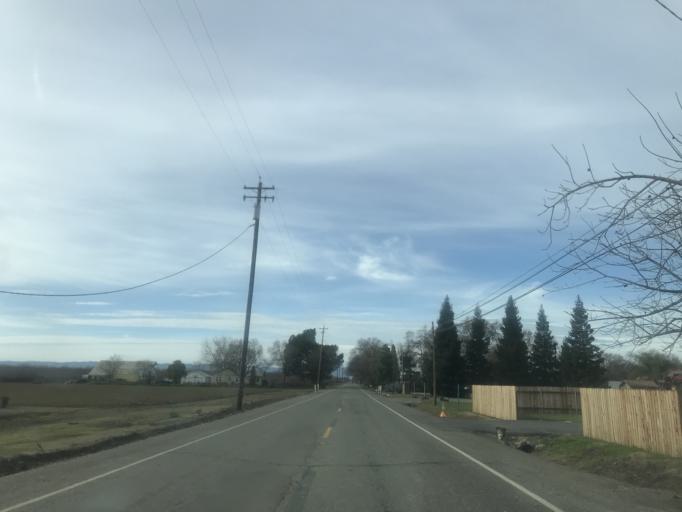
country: US
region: California
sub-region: Yolo County
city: Woodland
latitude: 38.6633
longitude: -121.8146
